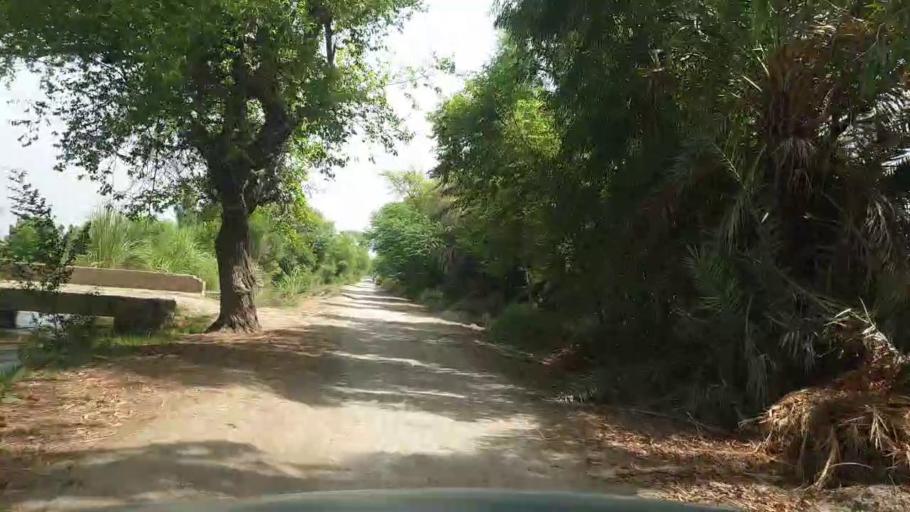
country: PK
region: Sindh
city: Garhi Yasin
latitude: 27.9506
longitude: 68.3787
